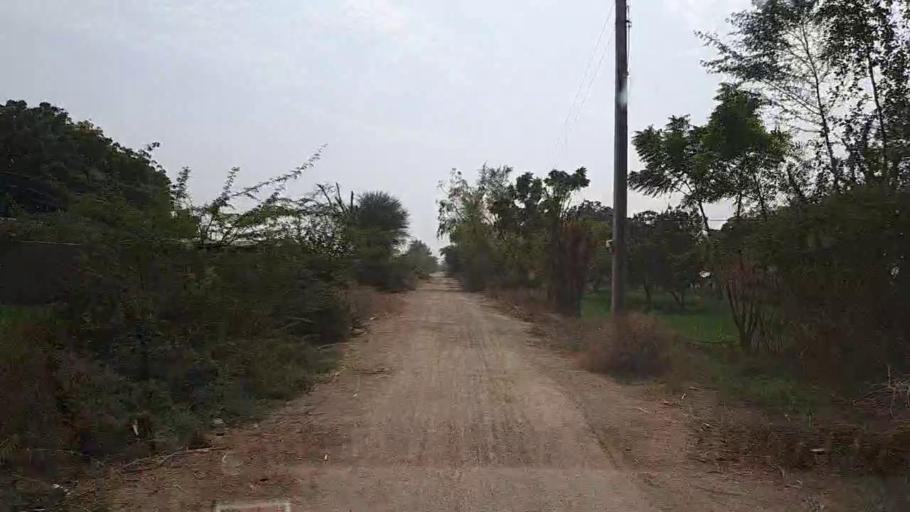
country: PK
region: Sindh
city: Mirwah Gorchani
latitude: 25.3451
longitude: 69.0786
